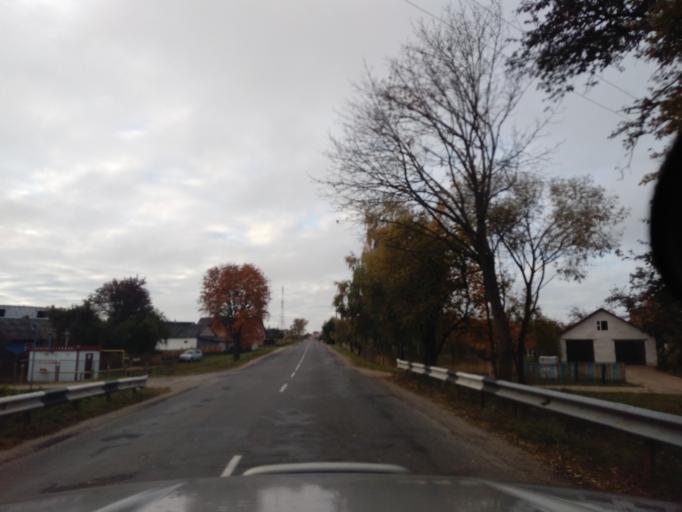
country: BY
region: Minsk
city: Kapyl'
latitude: 53.1566
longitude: 27.0765
